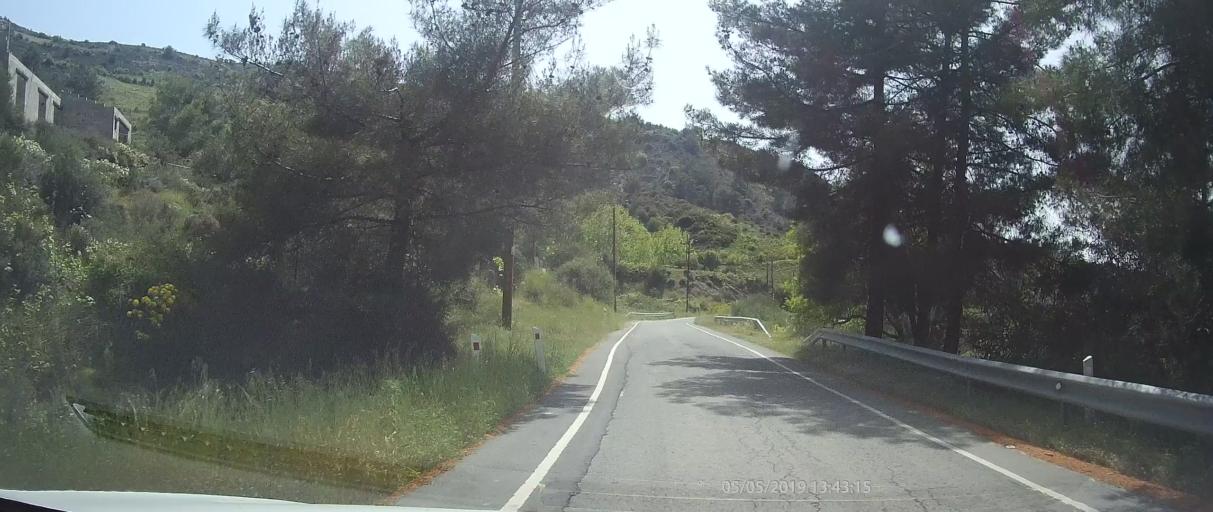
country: CY
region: Limassol
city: Pachna
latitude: 34.8732
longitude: 32.7997
